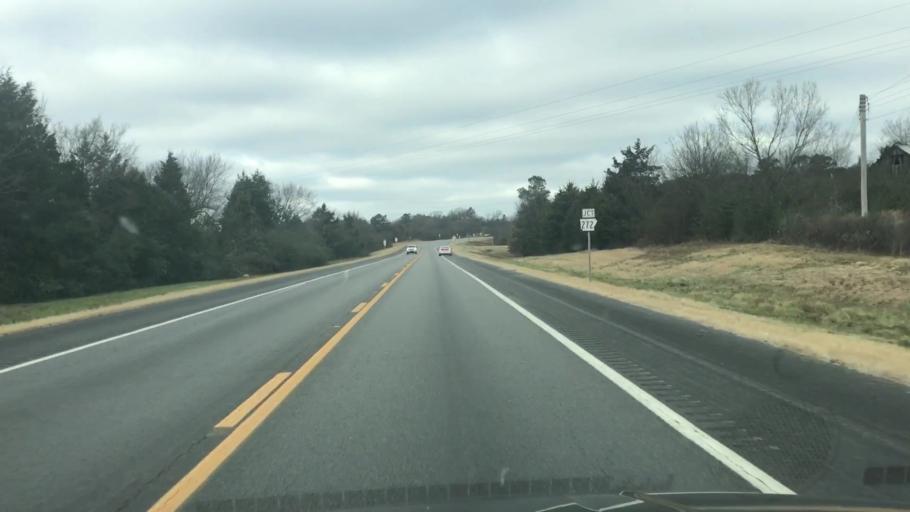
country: US
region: Arkansas
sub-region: Scott County
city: Waldron
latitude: 34.8805
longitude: -94.1010
